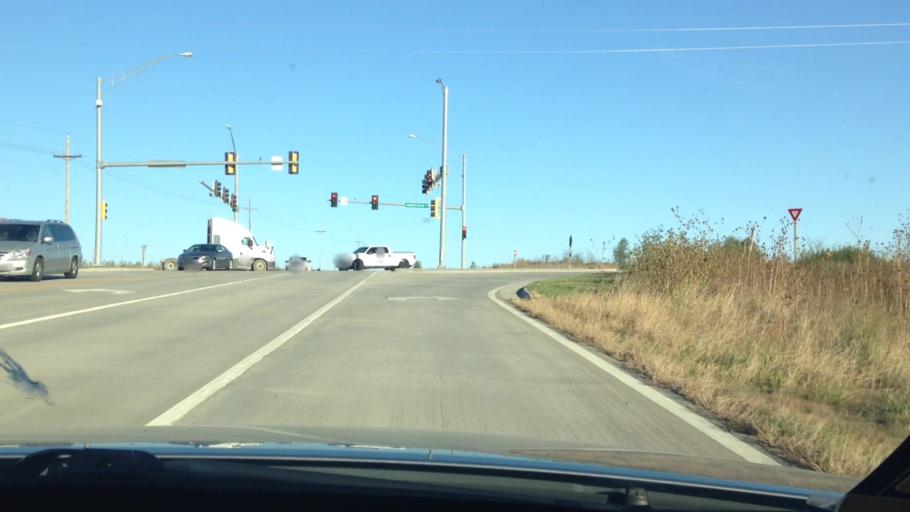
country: US
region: Kansas
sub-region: Johnson County
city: Edgerton
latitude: 38.7676
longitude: -94.9645
